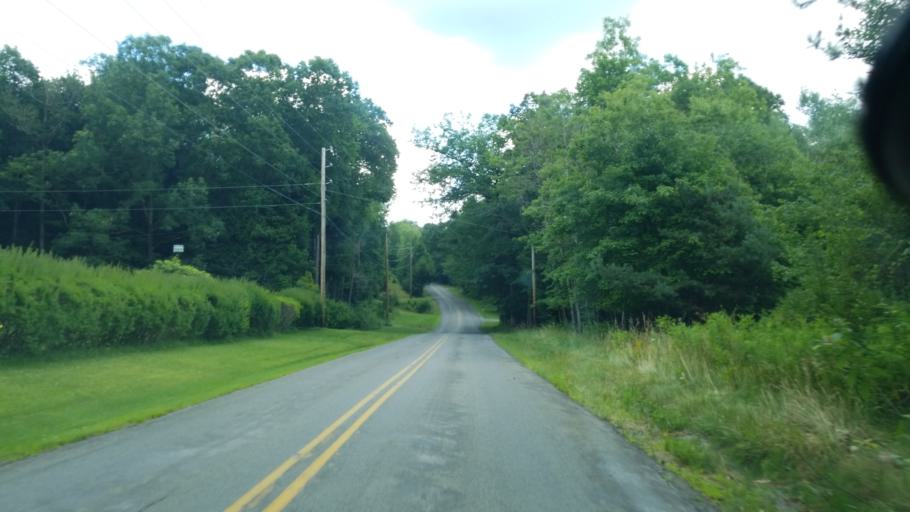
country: US
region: Pennsylvania
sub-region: Jefferson County
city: Brookville
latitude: 41.2313
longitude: -79.0638
